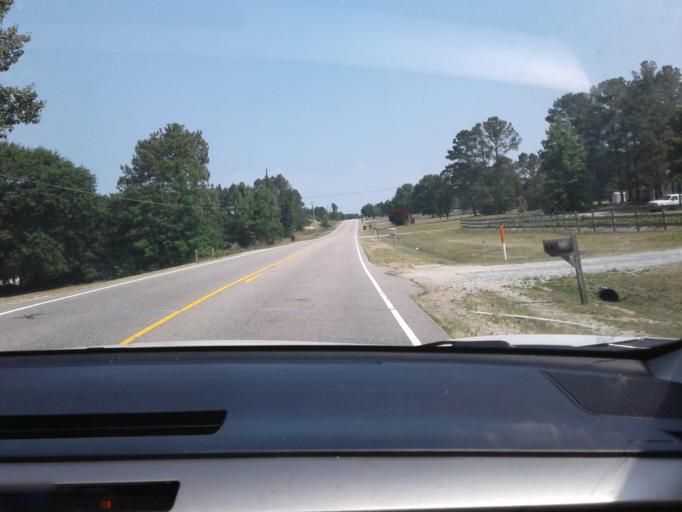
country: US
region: North Carolina
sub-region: Harnett County
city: Coats
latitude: 35.4552
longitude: -78.6894
